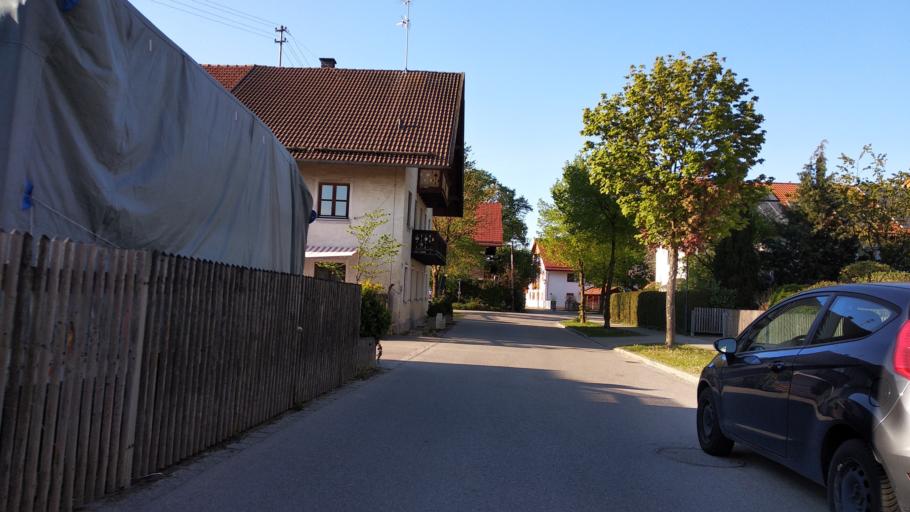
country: DE
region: Bavaria
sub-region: Upper Bavaria
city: Putzbrunn
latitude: 48.0842
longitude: 11.6960
